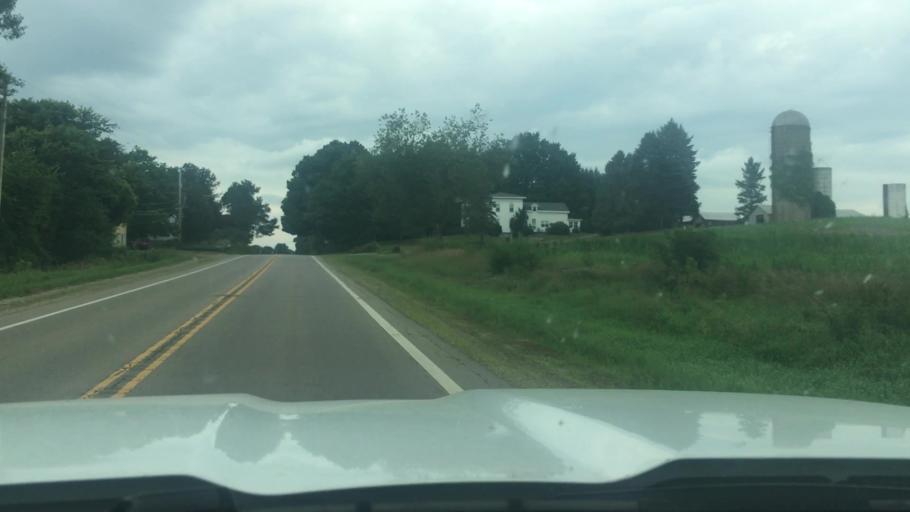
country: US
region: Michigan
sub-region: Ionia County
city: Ionia
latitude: 43.0018
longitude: -84.9608
